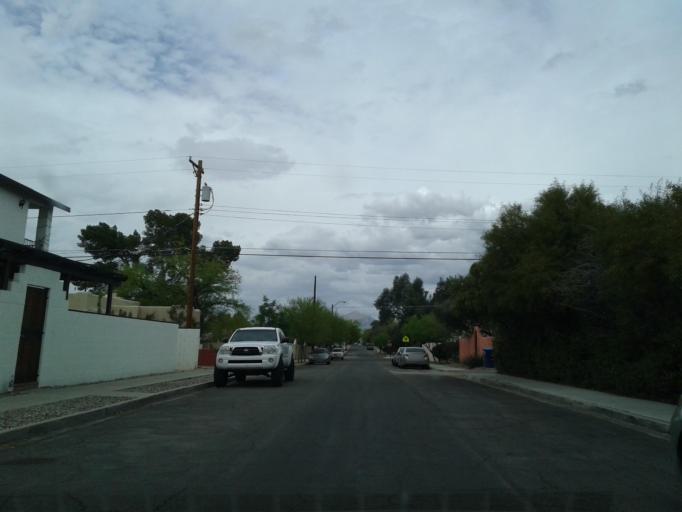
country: US
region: Arizona
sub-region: Pima County
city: Tucson
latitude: 32.2293
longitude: -110.9366
